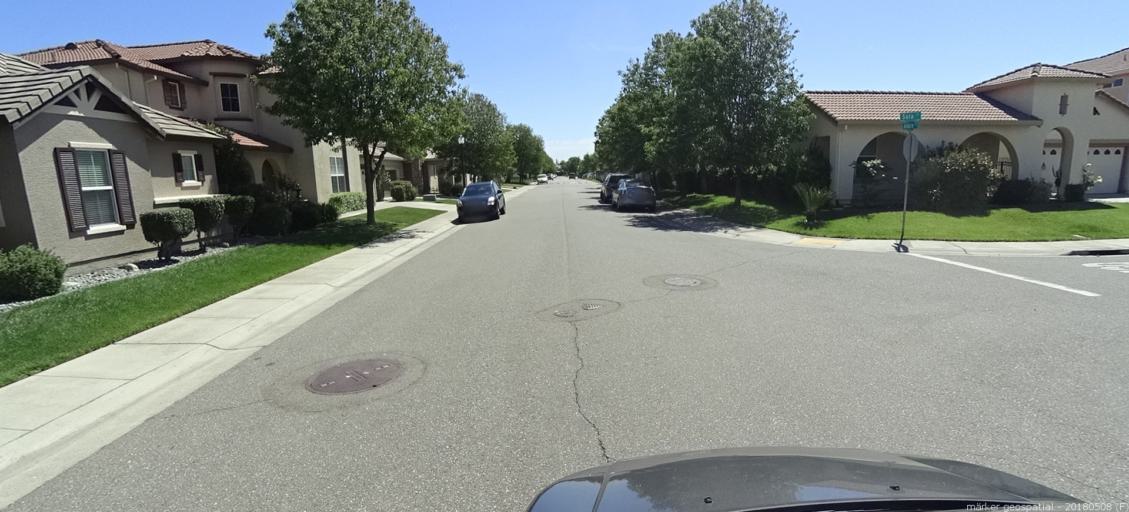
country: US
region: California
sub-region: Sacramento County
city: Elverta
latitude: 38.6831
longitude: -121.5372
